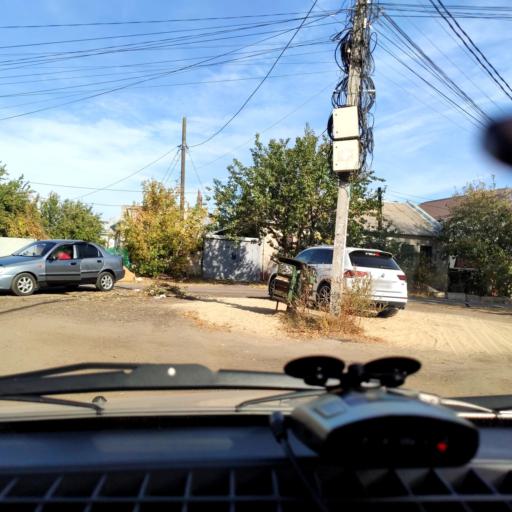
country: RU
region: Voronezj
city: Voronezh
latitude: 51.6880
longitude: 39.2261
